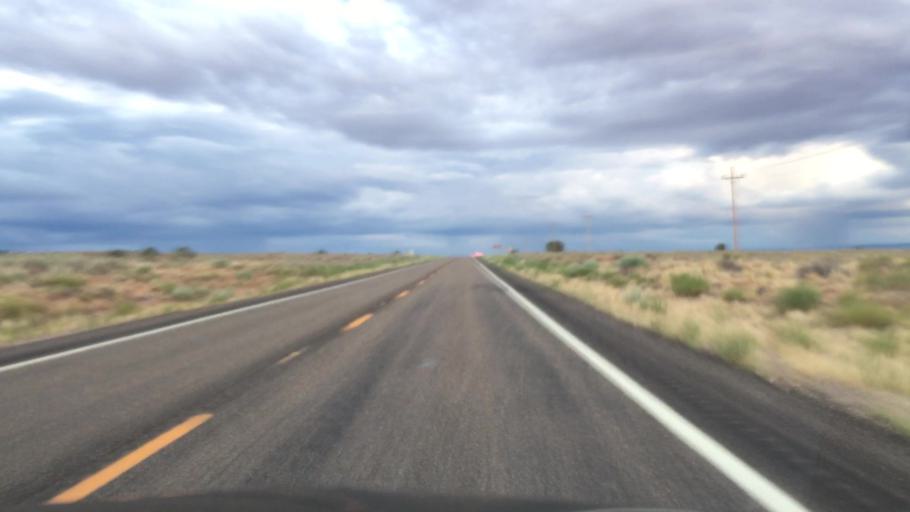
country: US
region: Arizona
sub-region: Coconino County
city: Fredonia
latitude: 36.8577
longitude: -112.7472
